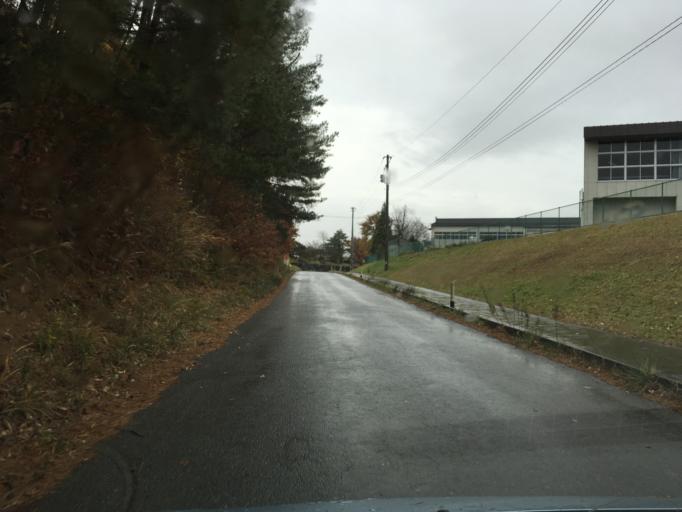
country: JP
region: Iwate
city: Ichinoseki
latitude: 38.7793
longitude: 141.2352
